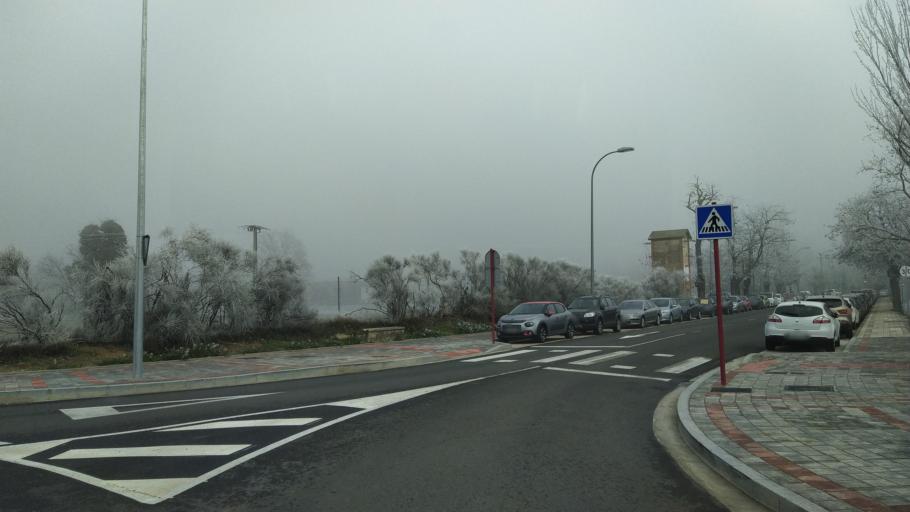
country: ES
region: Castille and Leon
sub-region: Provincia de Palencia
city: Palencia
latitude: 42.0019
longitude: -4.5384
